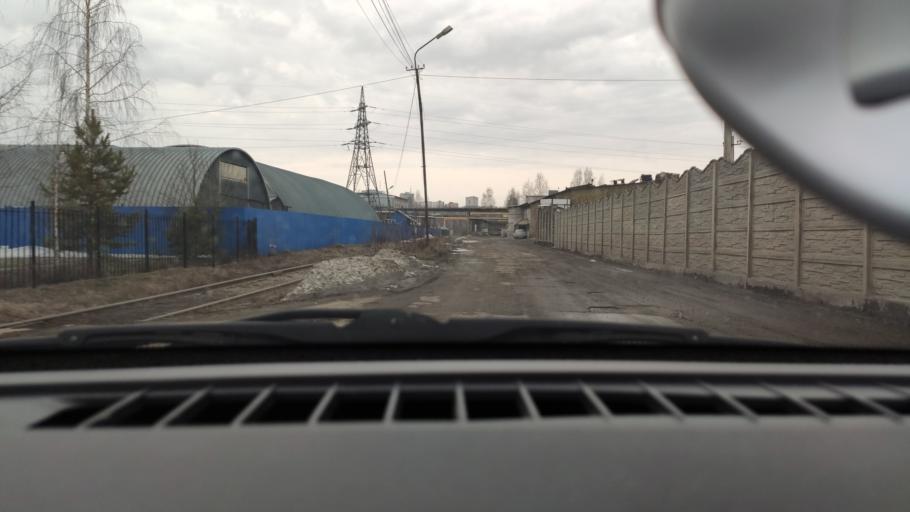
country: RU
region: Perm
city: Perm
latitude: 58.0437
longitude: 56.3127
